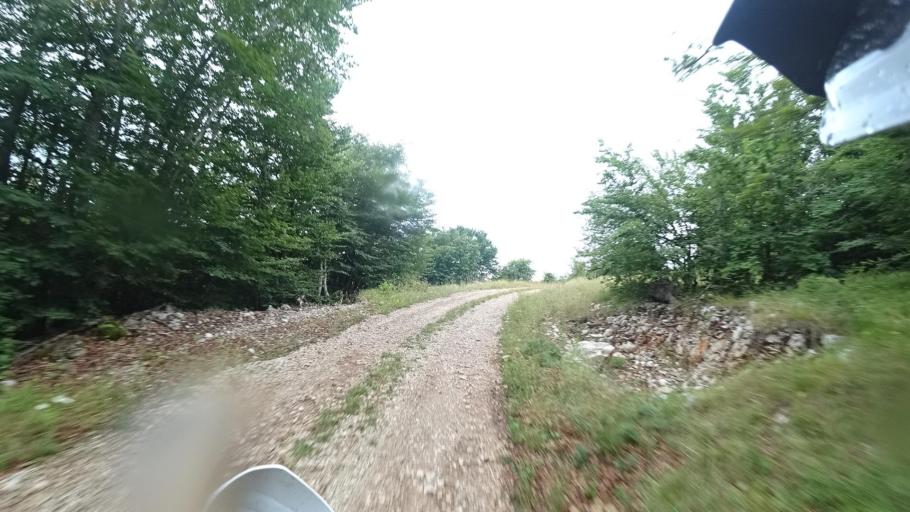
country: HR
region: Licko-Senjska
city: Jezerce
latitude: 44.7296
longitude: 15.6383
